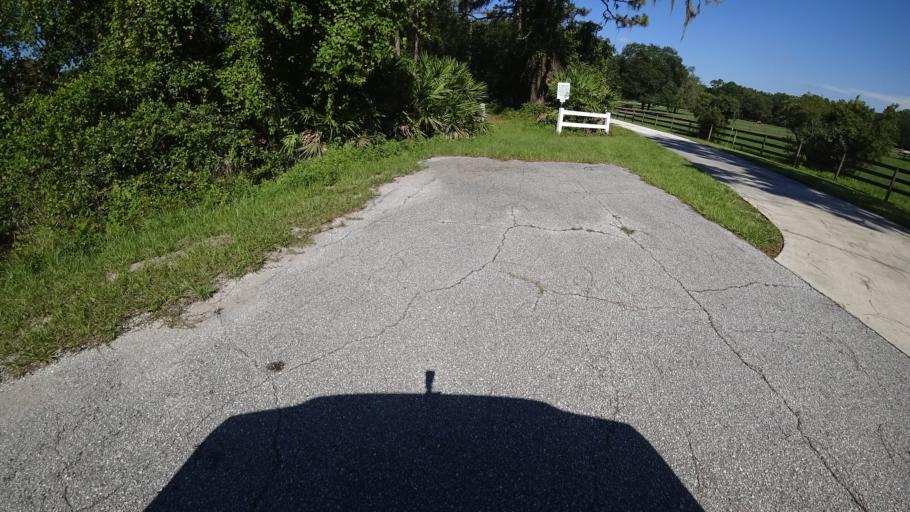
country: US
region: Florida
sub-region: Sarasota County
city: The Meadows
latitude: 27.4205
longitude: -82.3349
